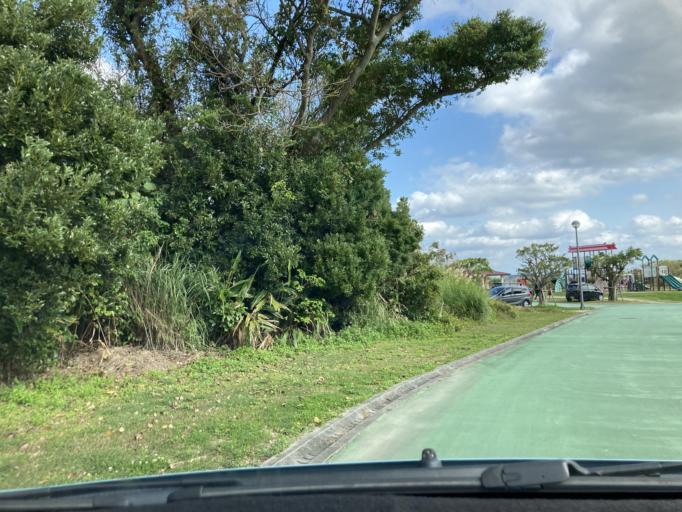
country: JP
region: Okinawa
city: Ginowan
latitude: 26.1873
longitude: 127.7633
